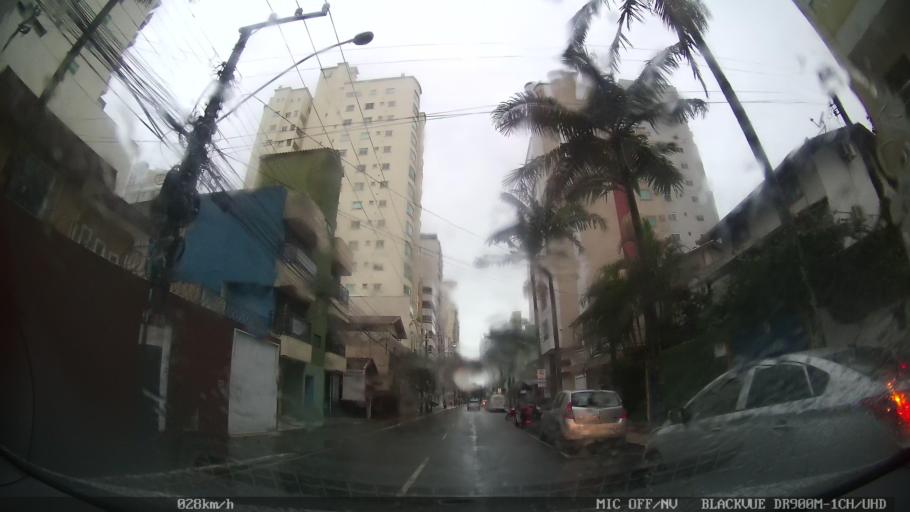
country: BR
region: Santa Catarina
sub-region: Balneario Camboriu
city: Balneario Camboriu
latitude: -26.9912
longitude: -48.6370
